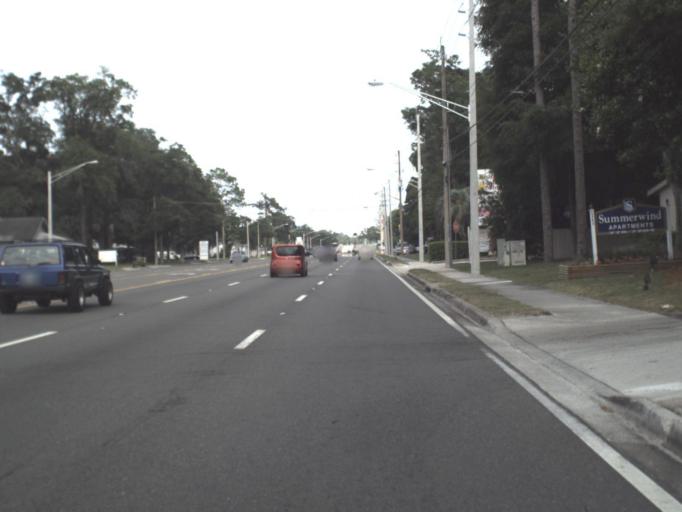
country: US
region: Florida
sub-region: Clay County
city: Bellair-Meadowbrook Terrace
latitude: 30.2474
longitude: -81.7185
